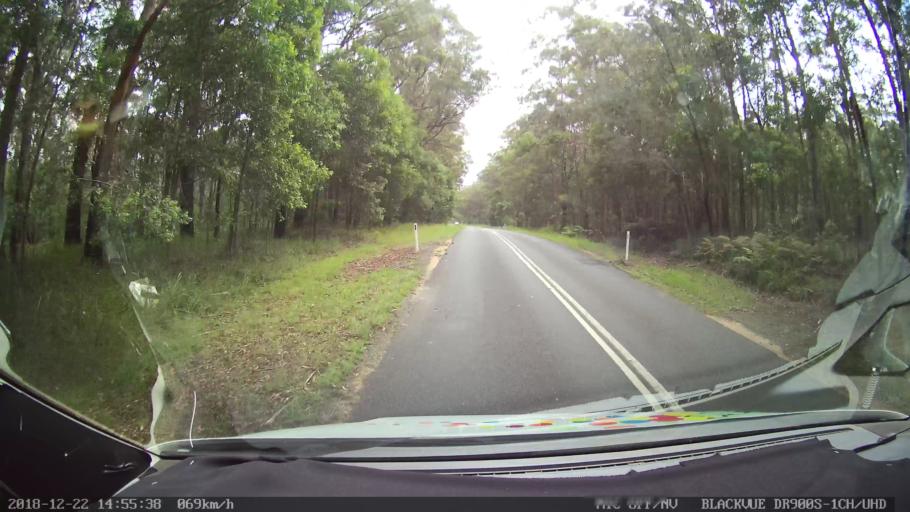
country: AU
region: New South Wales
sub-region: Bellingen
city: Dorrigo
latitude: -30.2305
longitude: 152.5194
